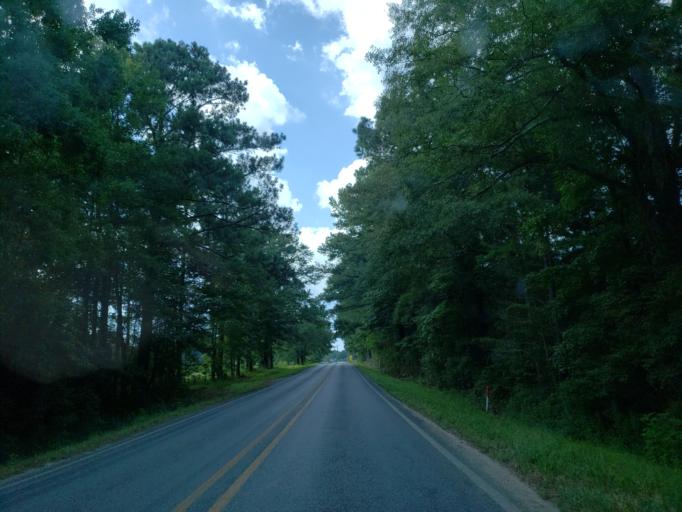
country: US
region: Mississippi
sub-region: Jones County
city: Sharon
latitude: 31.9154
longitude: -89.0191
